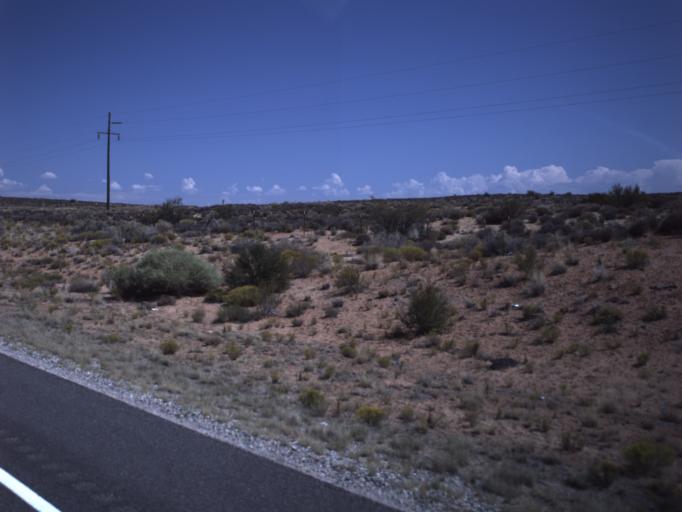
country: US
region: Utah
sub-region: San Juan County
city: Blanding
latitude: 37.3804
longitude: -109.5028
